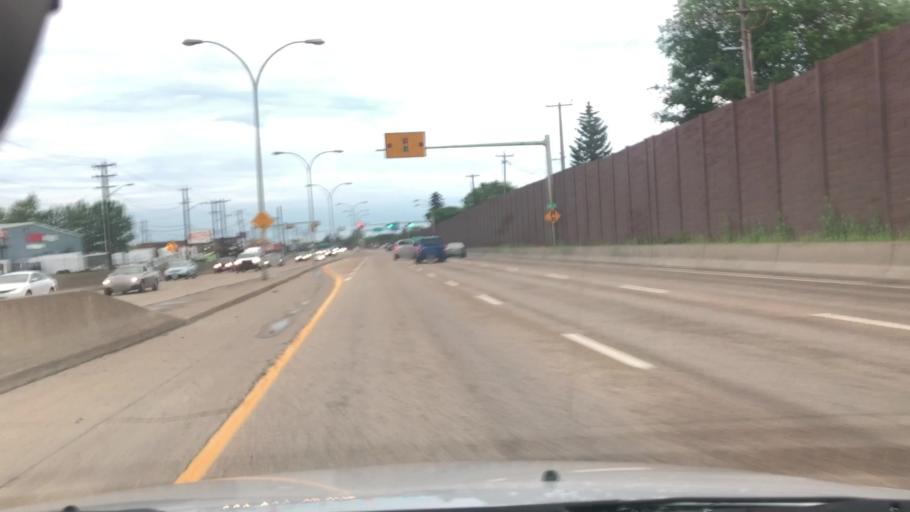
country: CA
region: Alberta
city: Edmonton
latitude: 53.5813
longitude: -113.4803
